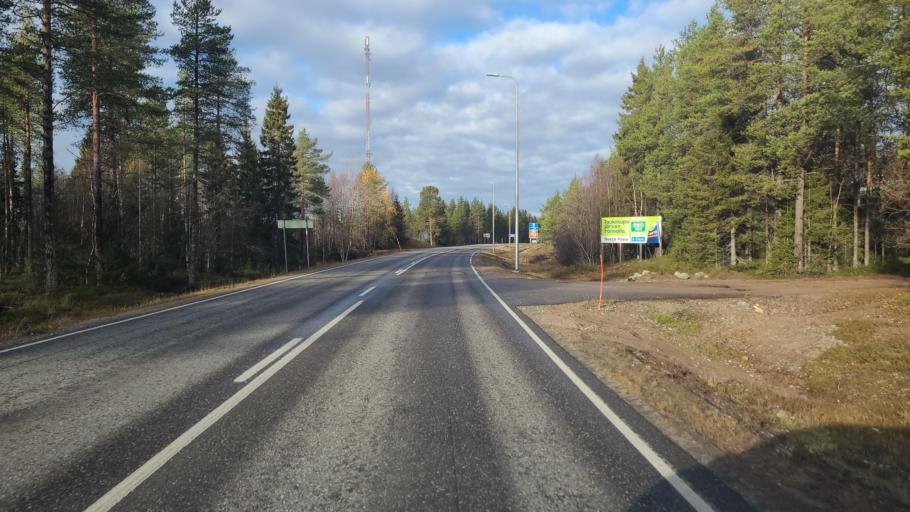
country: FI
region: Lapland
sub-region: Itae-Lappi
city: Posio
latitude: 66.1041
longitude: 28.1863
